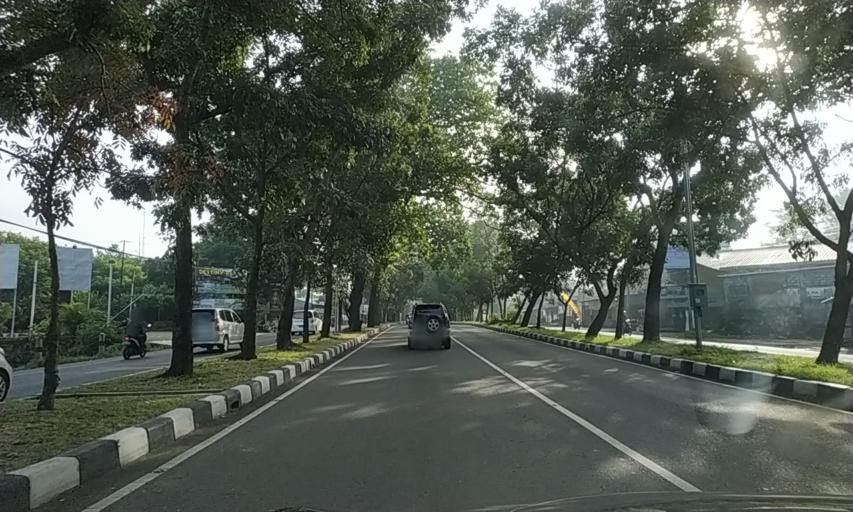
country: ID
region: Central Java
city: Candi Prambanan
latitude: -7.7592
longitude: 110.4784
